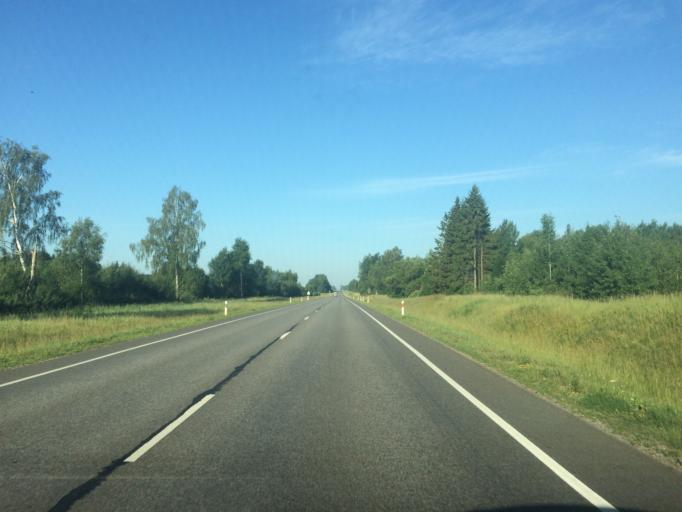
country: LT
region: Vilnius County
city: Ukmerge
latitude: 55.1781
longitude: 24.5529
